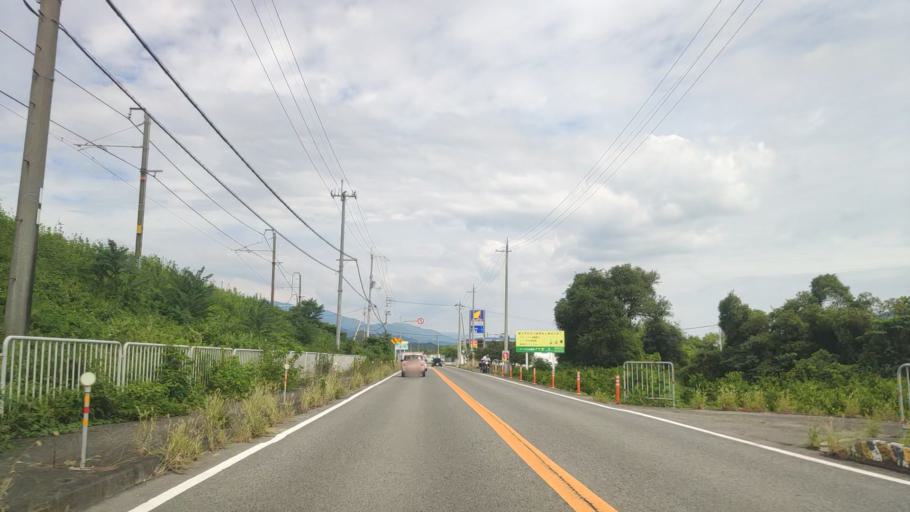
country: JP
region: Wakayama
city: Iwade
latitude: 34.2814
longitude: 135.4579
